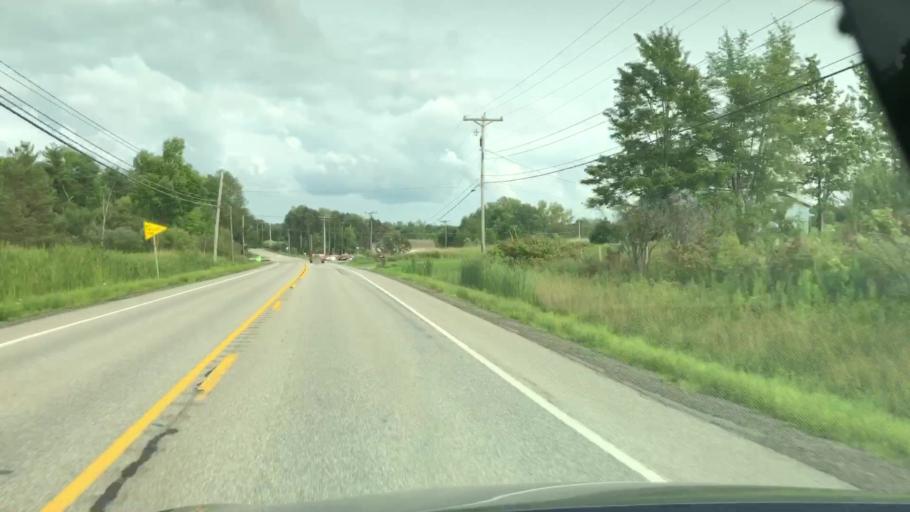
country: US
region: Pennsylvania
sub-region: Erie County
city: Northwest Harborcreek
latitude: 42.0644
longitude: -79.9438
